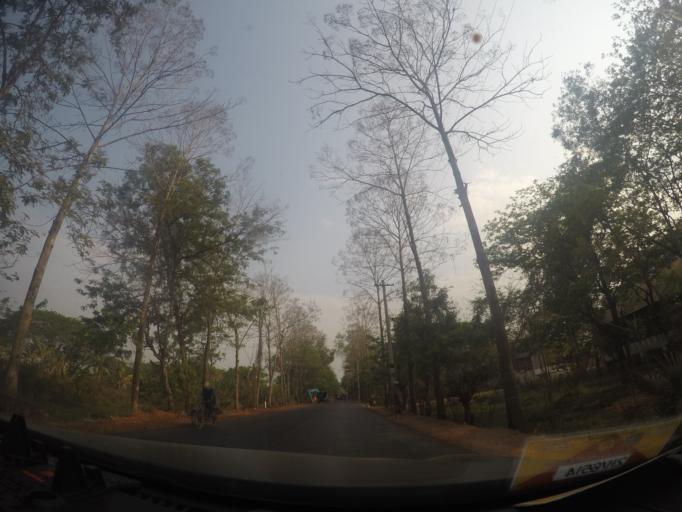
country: MM
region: Bago
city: Paungde
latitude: 18.3216
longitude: 95.6278
